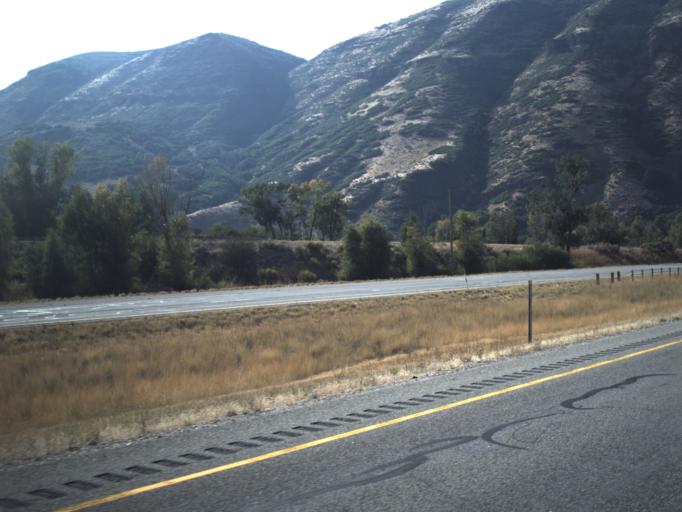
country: US
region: Utah
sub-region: Morgan County
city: Morgan
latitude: 41.0409
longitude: -111.5178
